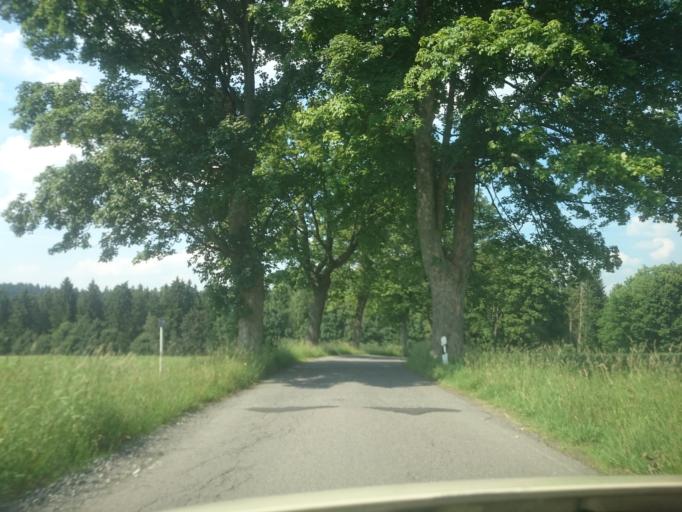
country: DE
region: Saxony
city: Lengefeld
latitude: 50.7491
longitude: 13.2142
